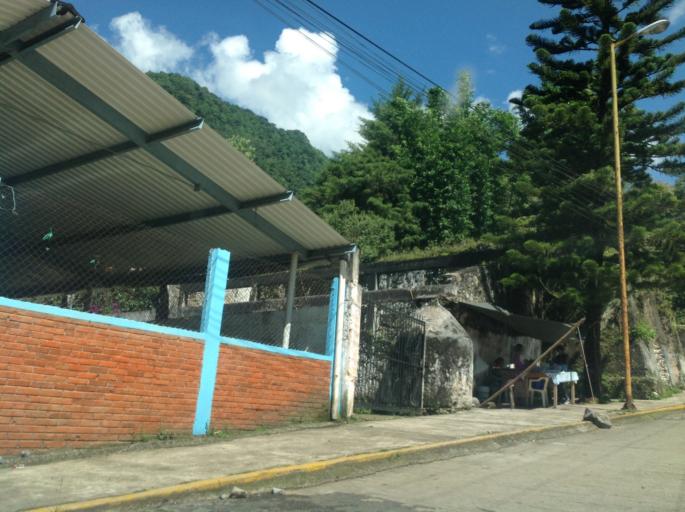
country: MX
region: Veracruz
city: Nogales
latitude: 18.8433
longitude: -97.1608
